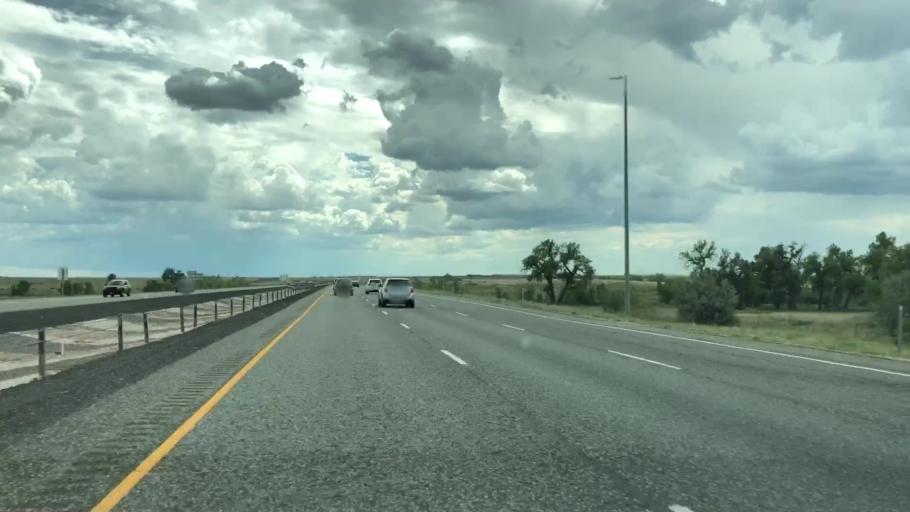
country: US
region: Colorado
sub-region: Adams County
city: Aurora
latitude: 39.7157
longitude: -104.7228
